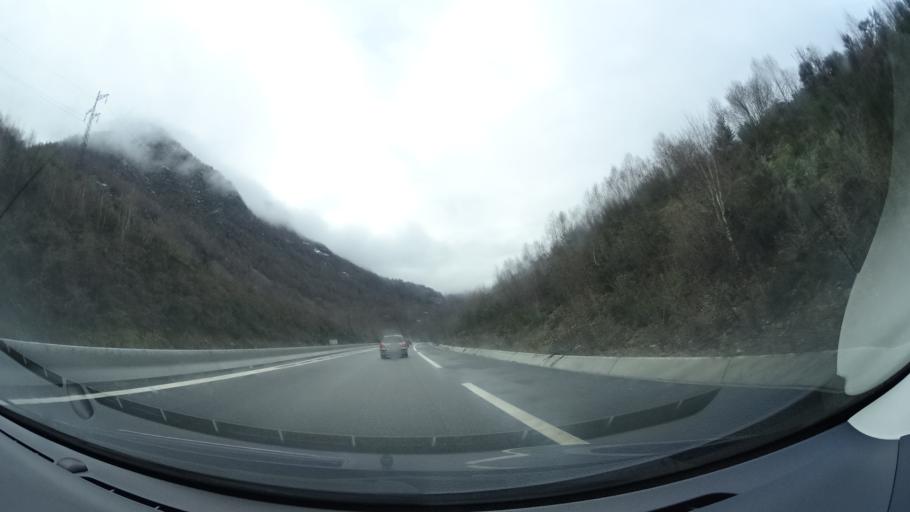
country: FR
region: Midi-Pyrenees
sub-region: Departement de l'Ariege
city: Ax-les-Thermes
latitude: 42.7337
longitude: 1.7960
